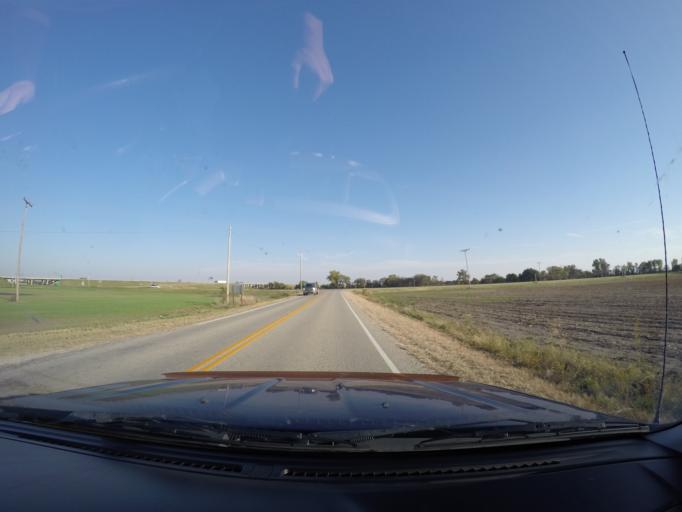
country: US
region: Kansas
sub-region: Saline County
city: Salina
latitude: 38.8407
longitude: -97.6502
